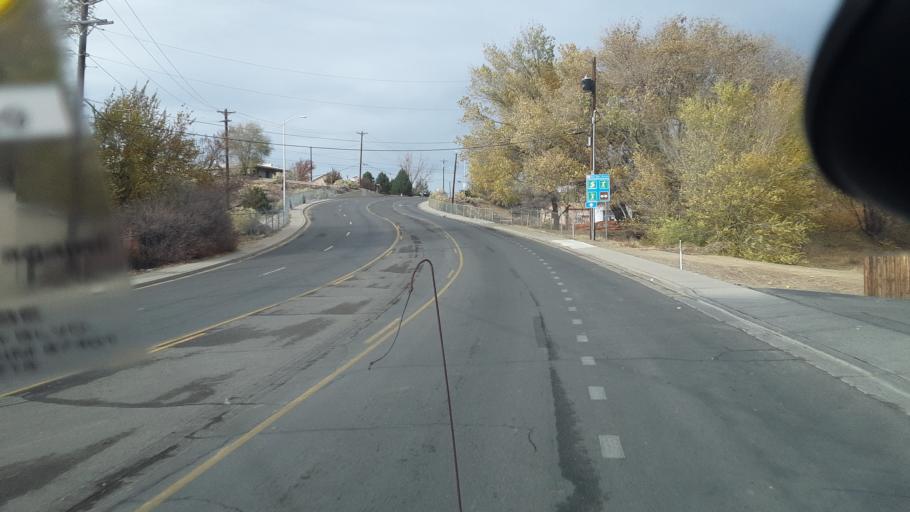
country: US
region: New Mexico
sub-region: San Juan County
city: Farmington
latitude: 36.7315
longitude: -108.1975
